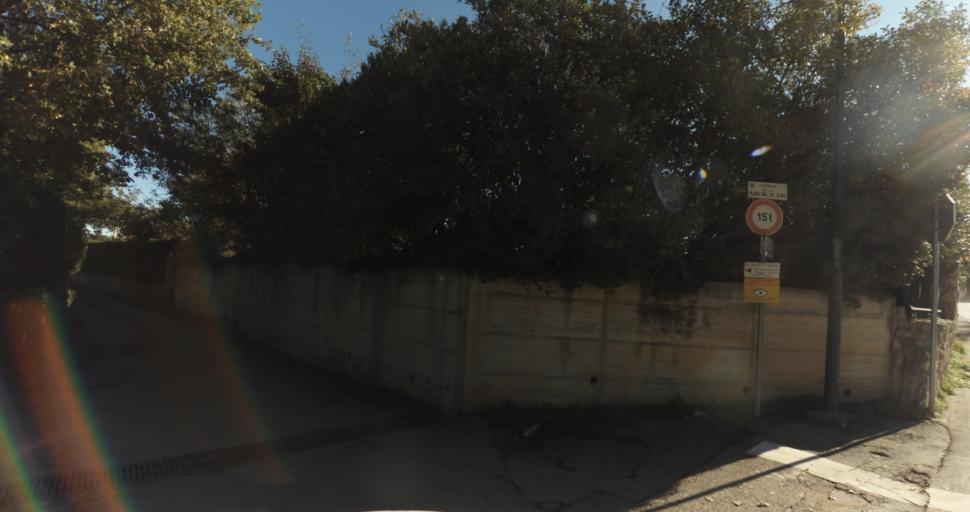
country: FR
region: Provence-Alpes-Cote d'Azur
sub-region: Departement des Alpes-Maritimes
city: Vence
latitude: 43.7151
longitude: 7.0863
